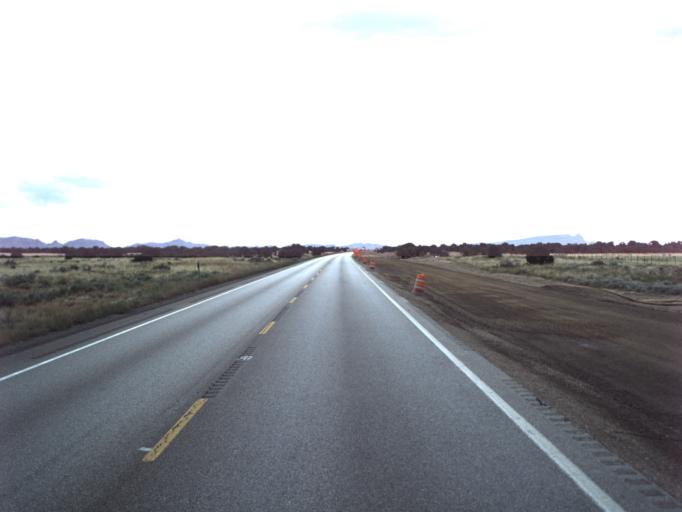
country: US
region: Utah
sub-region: Carbon County
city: East Carbon City
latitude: 39.4254
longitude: -110.4462
